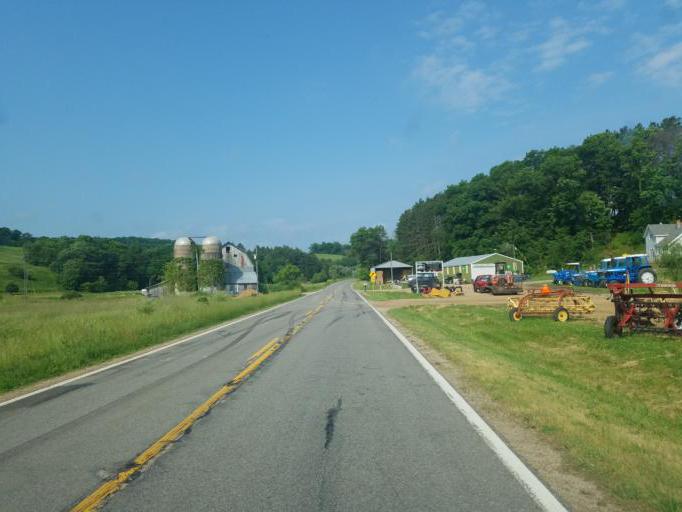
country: US
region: Wisconsin
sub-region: Vernon County
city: Hillsboro
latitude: 43.6842
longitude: -90.5534
